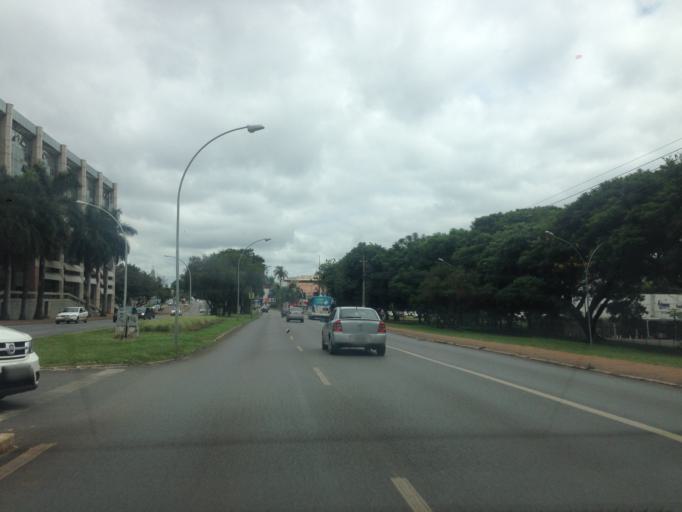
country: BR
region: Federal District
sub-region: Brasilia
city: Brasilia
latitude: -15.7849
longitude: -47.8876
